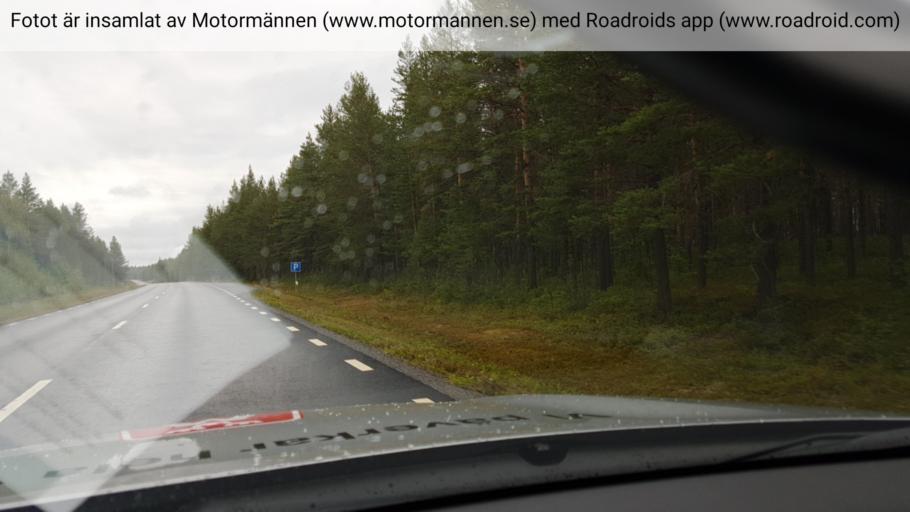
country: SE
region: Norrbotten
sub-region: Alvsbyns Kommun
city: AElvsbyn
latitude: 66.2499
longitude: 20.8546
